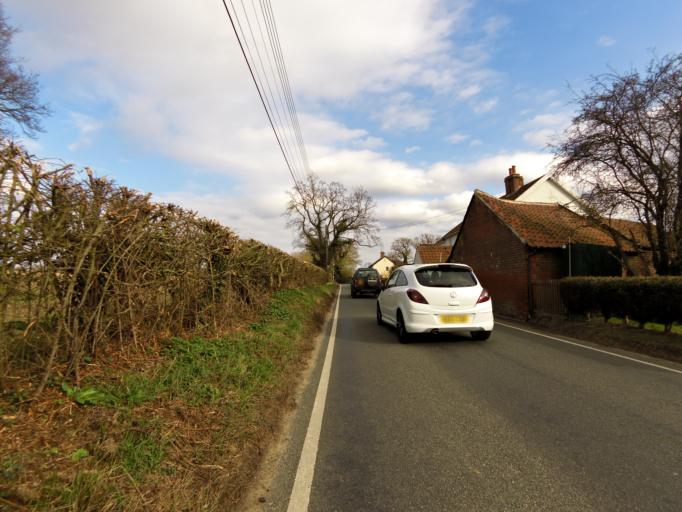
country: GB
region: England
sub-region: Suffolk
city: Ipswich
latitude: 52.0862
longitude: 1.1654
